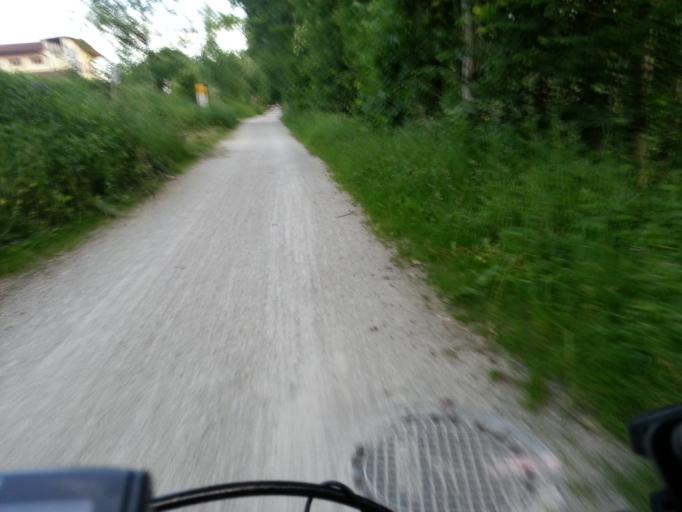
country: AT
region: Salzburg
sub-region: Politischer Bezirk Salzburg-Umgebung
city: Elsbethen
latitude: 47.7518
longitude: 13.0804
